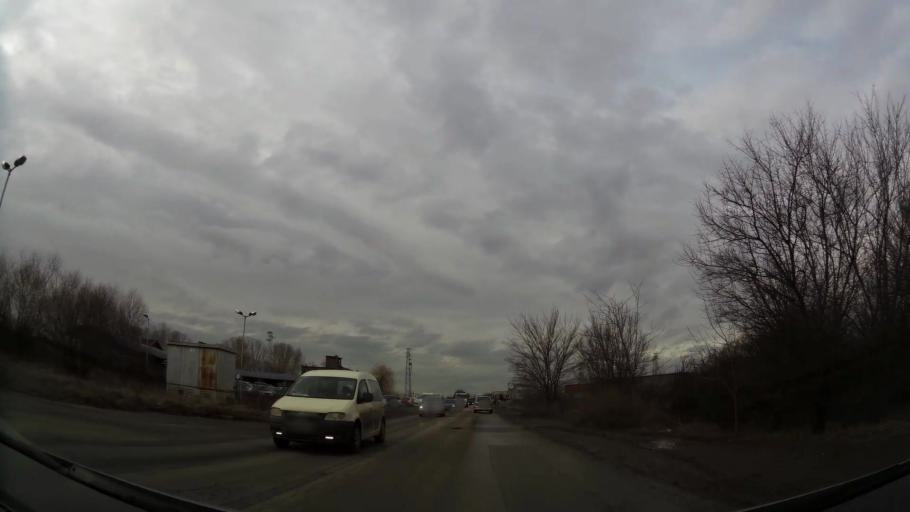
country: BG
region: Sofia-Capital
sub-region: Stolichna Obshtina
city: Sofia
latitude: 42.7525
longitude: 23.2743
